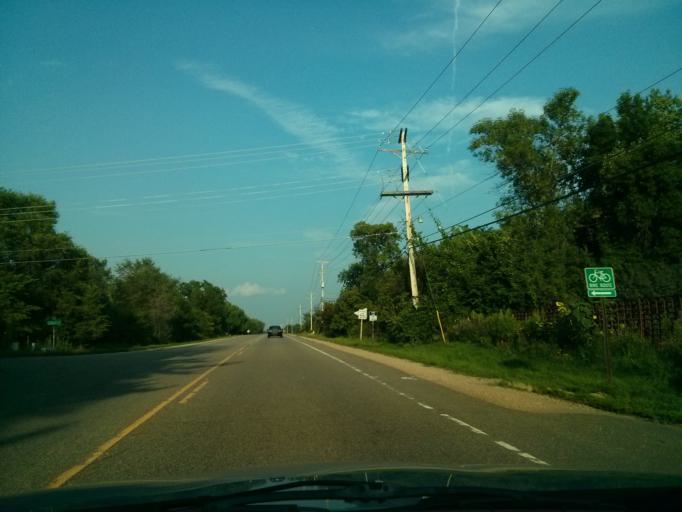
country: US
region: Wisconsin
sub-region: Saint Croix County
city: North Hudson
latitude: 44.9924
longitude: -92.7012
